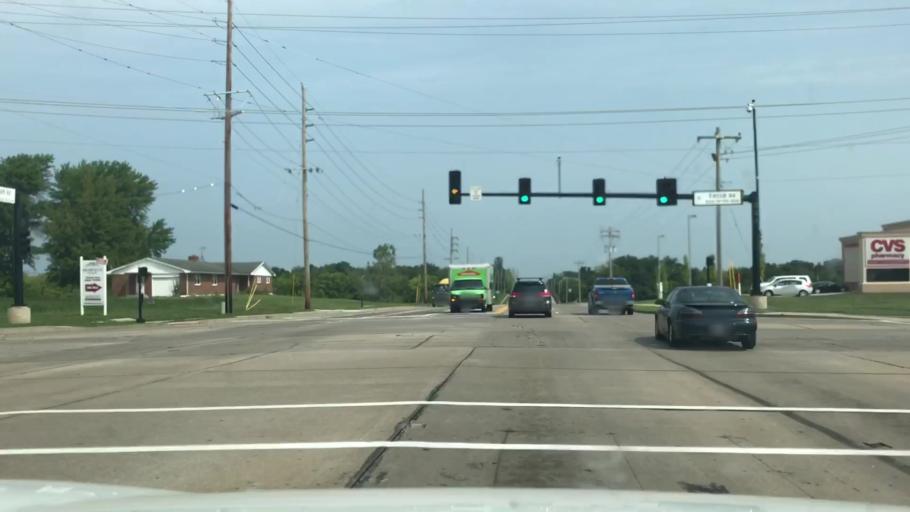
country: US
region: Missouri
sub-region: Saint Charles County
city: Dardenne Prairie
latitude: 38.7730
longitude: -90.7375
